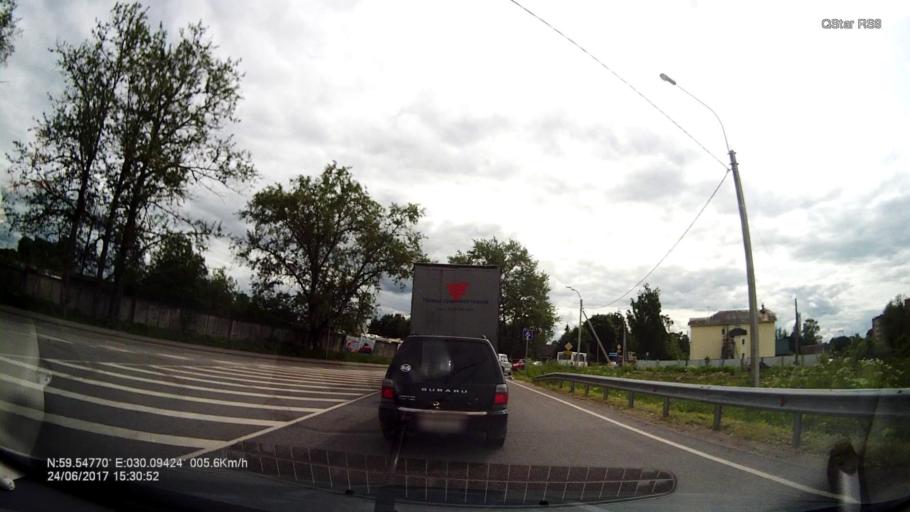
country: RU
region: Leningrad
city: Mariyenburg
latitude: 59.5476
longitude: 30.0942
